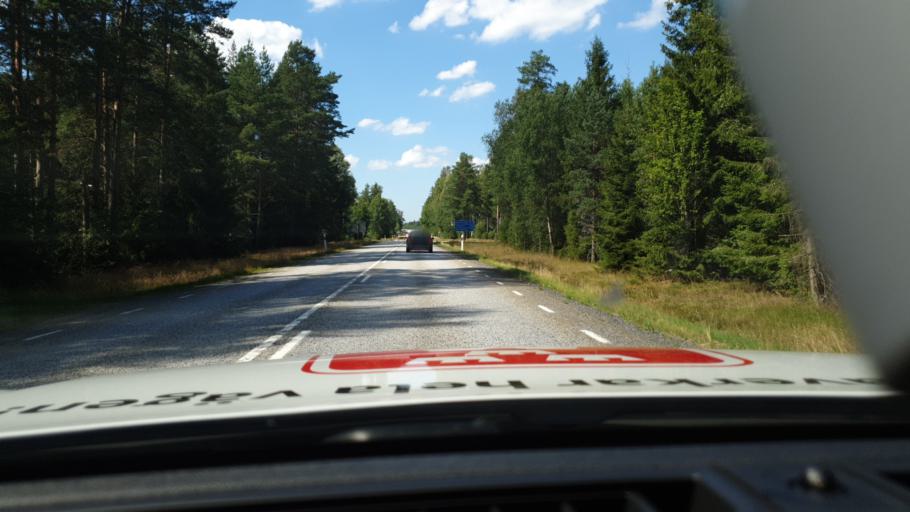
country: SE
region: Joenkoeping
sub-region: Jonkopings Kommun
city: Odensjo
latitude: 57.6073
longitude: 14.2159
